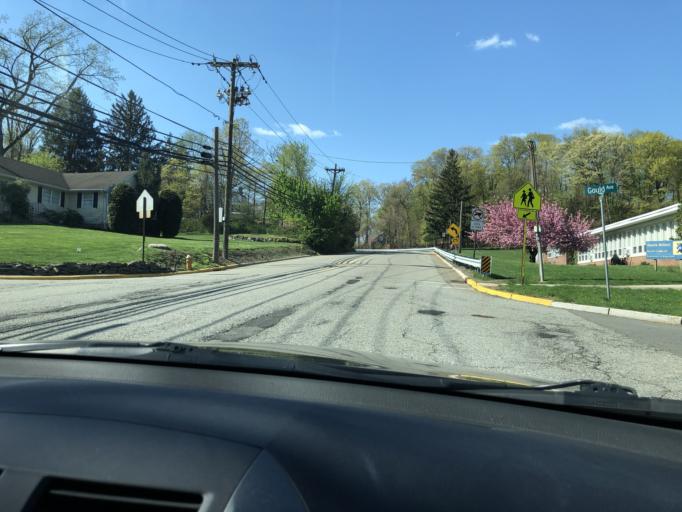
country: US
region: New Jersey
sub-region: Essex County
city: North Caldwell
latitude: 40.8593
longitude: -74.2586
